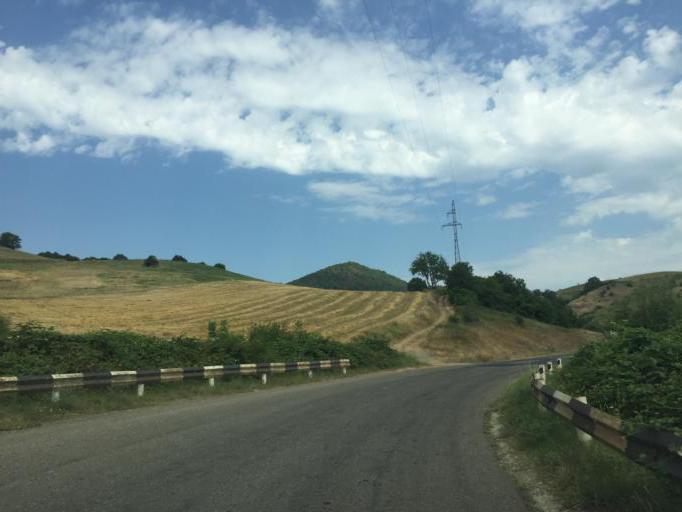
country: AZ
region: Xocali
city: Xocali
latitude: 39.9840
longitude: 46.6899
